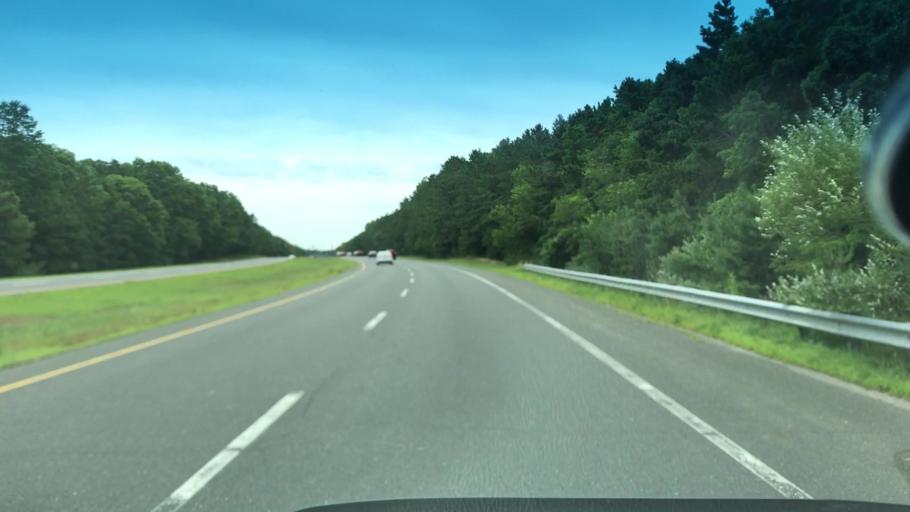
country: US
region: New York
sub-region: Suffolk County
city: Yaphank
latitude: 40.8554
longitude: -72.9004
